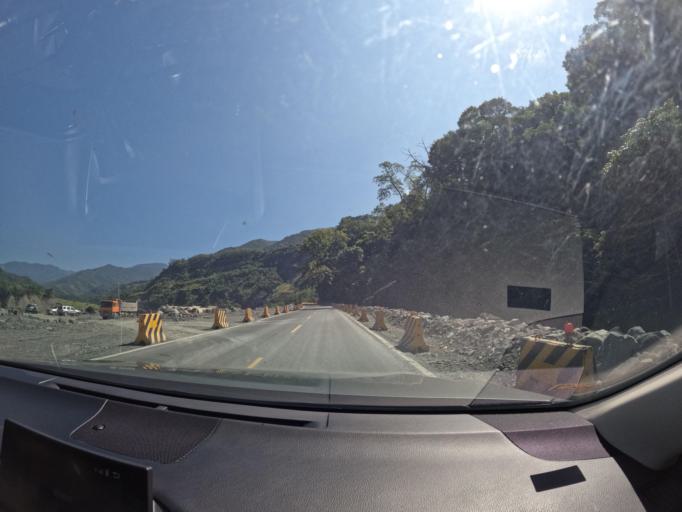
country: TW
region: Taiwan
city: Yujing
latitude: 23.1870
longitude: 120.7863
